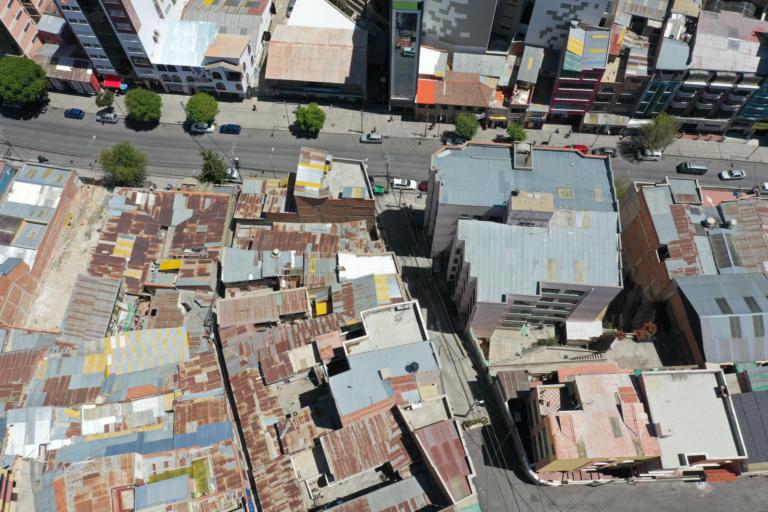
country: BO
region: La Paz
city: La Paz
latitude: -16.5008
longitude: -68.1257
